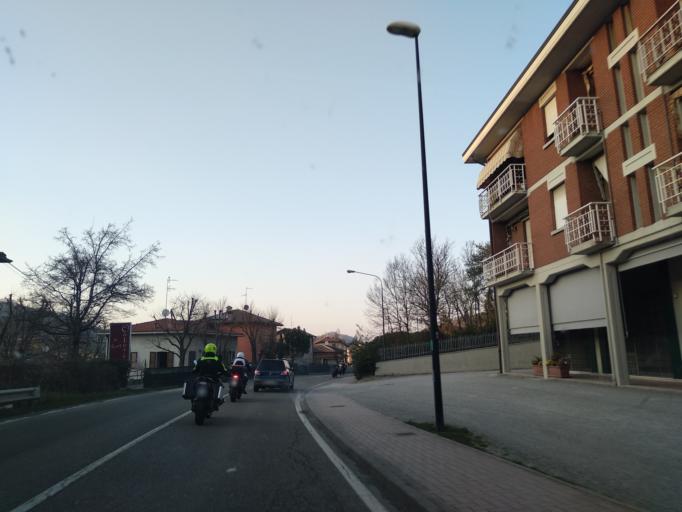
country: IT
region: Emilia-Romagna
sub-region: Provincia di Reggio Emilia
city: Vezzano sul Crostolo
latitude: 44.5624
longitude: 10.5285
